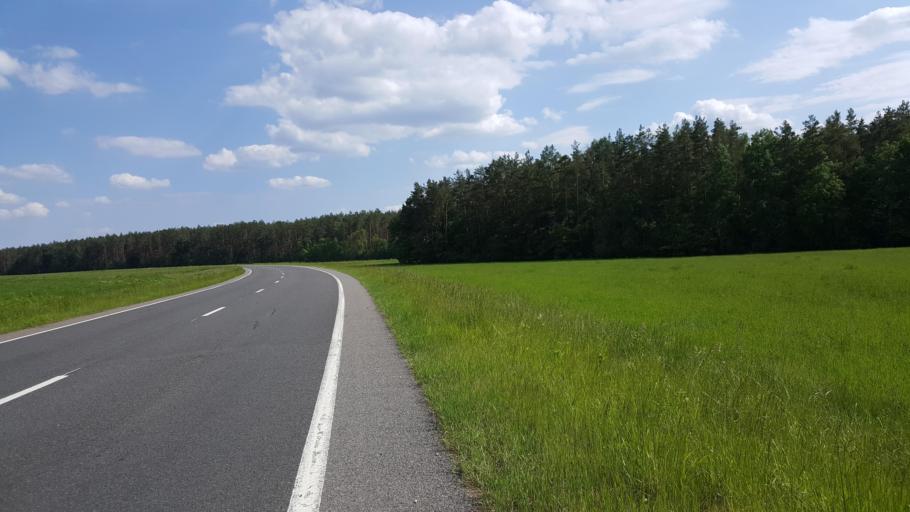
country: PL
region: Podlasie
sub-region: Powiat hajnowski
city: Bialowieza
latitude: 52.5538
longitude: 24.1374
